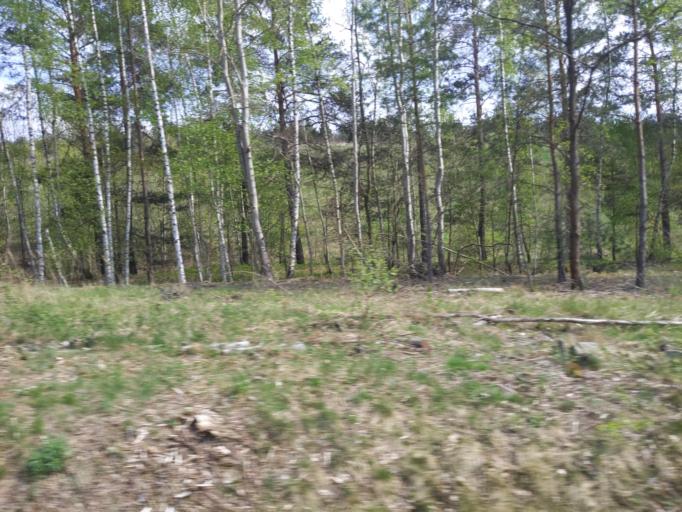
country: DE
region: Saxony
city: Albertstadt
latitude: 51.1255
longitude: 13.8009
